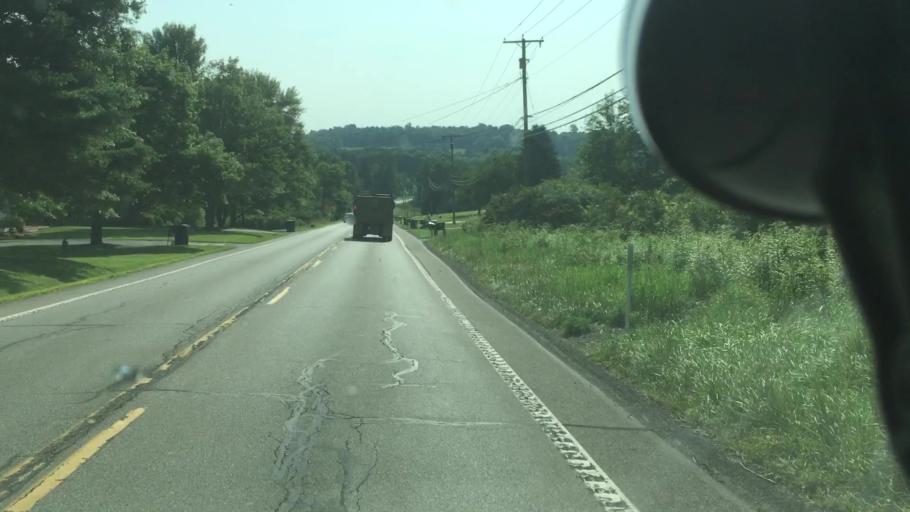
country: US
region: Pennsylvania
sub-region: Lawrence County
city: New Castle
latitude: 41.0132
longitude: -80.2510
